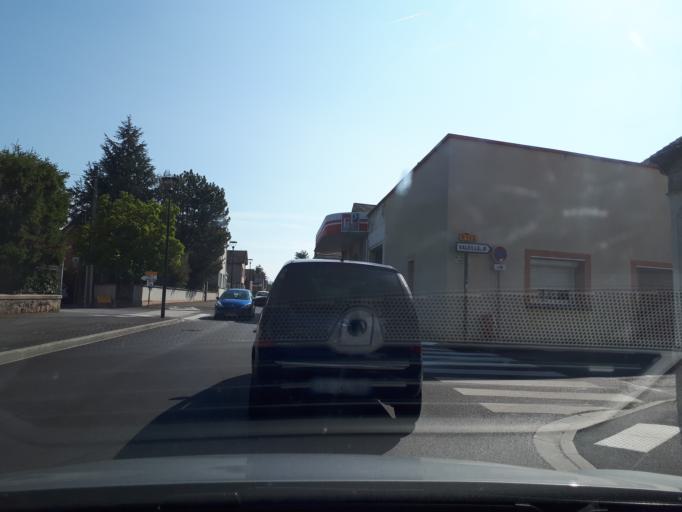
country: FR
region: Rhone-Alpes
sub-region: Departement de la Loire
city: Feurs
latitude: 45.7442
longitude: 4.2326
